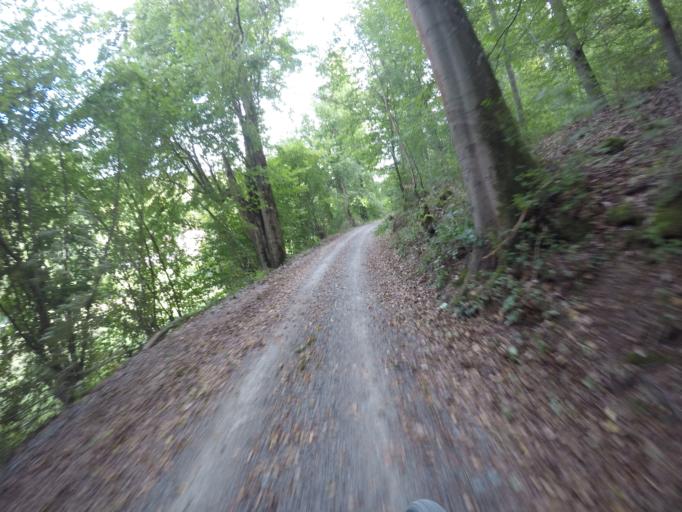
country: DE
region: Baden-Wuerttemberg
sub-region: Regierungsbezirk Stuttgart
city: Eberdingen
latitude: 48.8609
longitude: 8.9628
